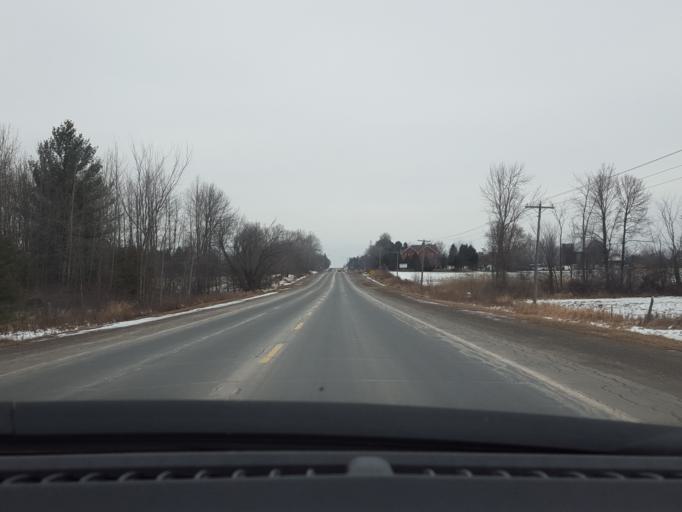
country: CA
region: Ontario
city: Newmarket
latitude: 44.1208
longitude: -79.4201
